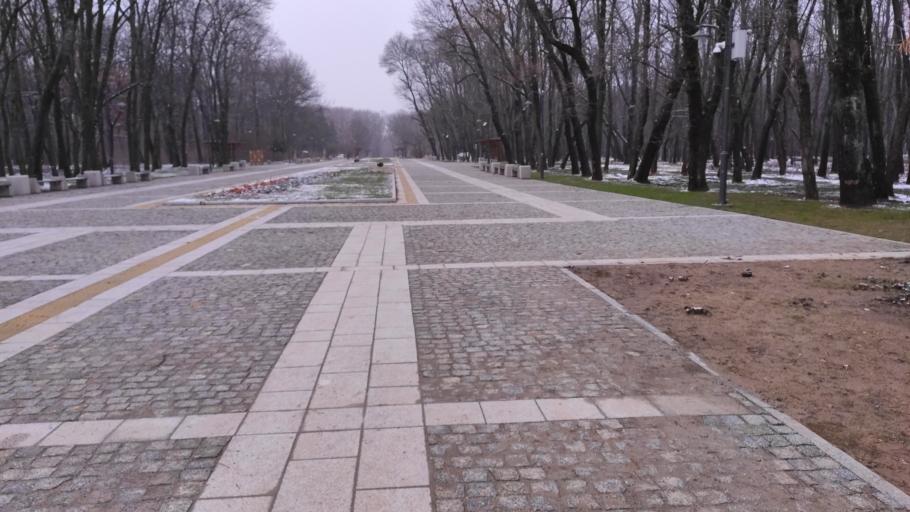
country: BG
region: Sofia-Capital
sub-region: Stolichna Obshtina
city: Sofia
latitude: 42.7114
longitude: 23.2823
